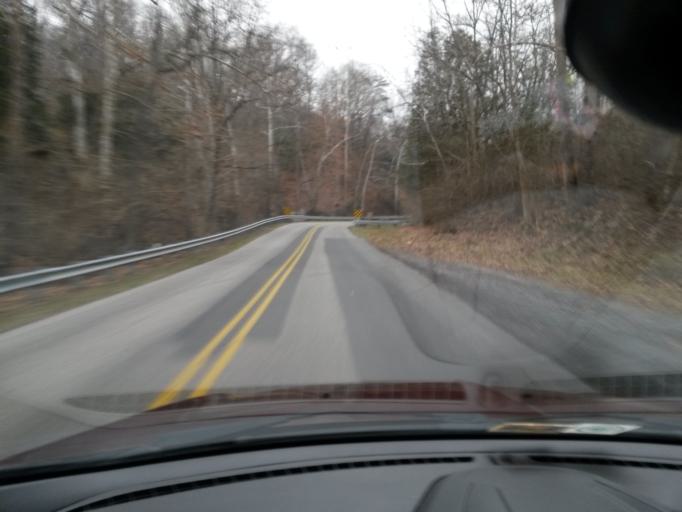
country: US
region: Virginia
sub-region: Rockbridge County
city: East Lexington
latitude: 37.8951
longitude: -79.3559
